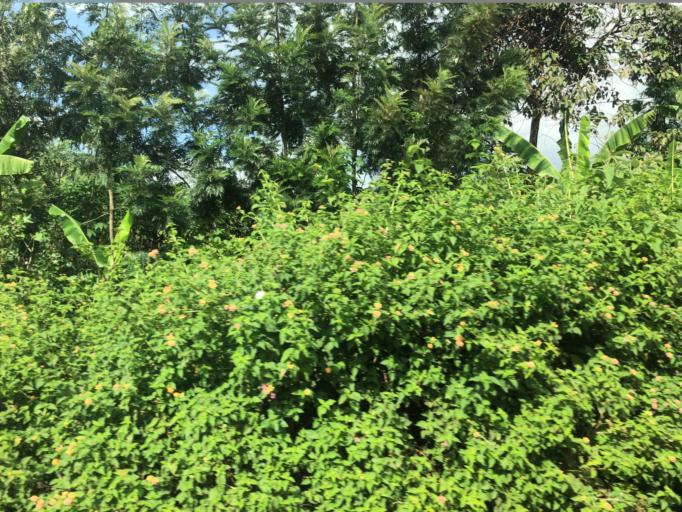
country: ET
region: Southern Nations, Nationalities, and People's Region
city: Bako
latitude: 5.7441
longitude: 36.5981
